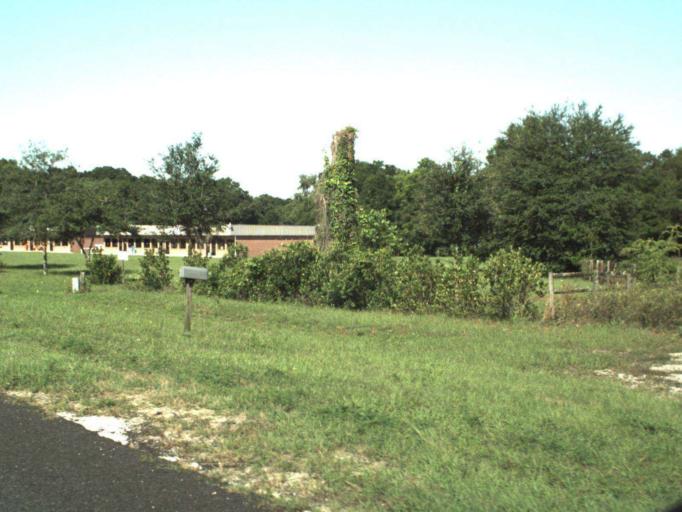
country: US
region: Florida
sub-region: Marion County
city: Citra
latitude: 29.3982
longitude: -82.1160
